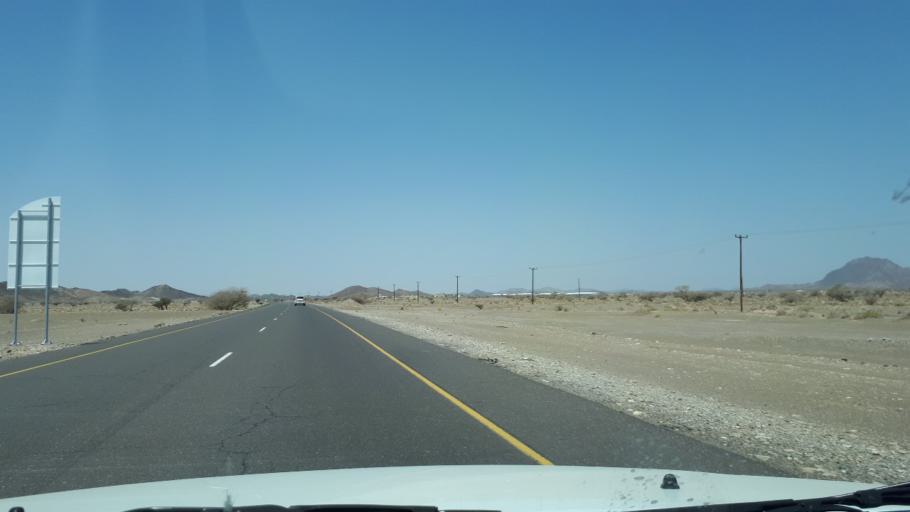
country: OM
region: Ash Sharqiyah
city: Ibra'
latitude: 22.6413
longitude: 58.4886
